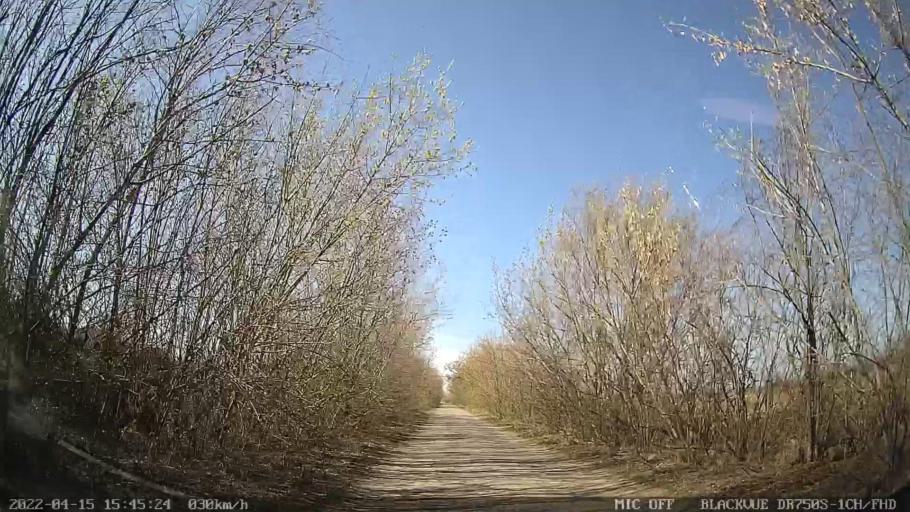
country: MD
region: Raionul Ocnita
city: Otaci
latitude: 48.3761
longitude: 27.9184
